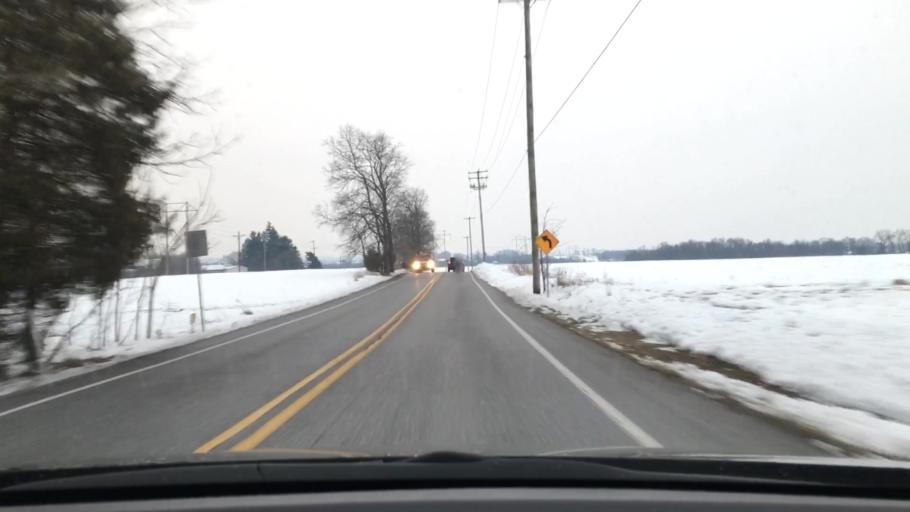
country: US
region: Pennsylvania
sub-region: York County
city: Weigelstown
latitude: 39.9690
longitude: -76.8470
